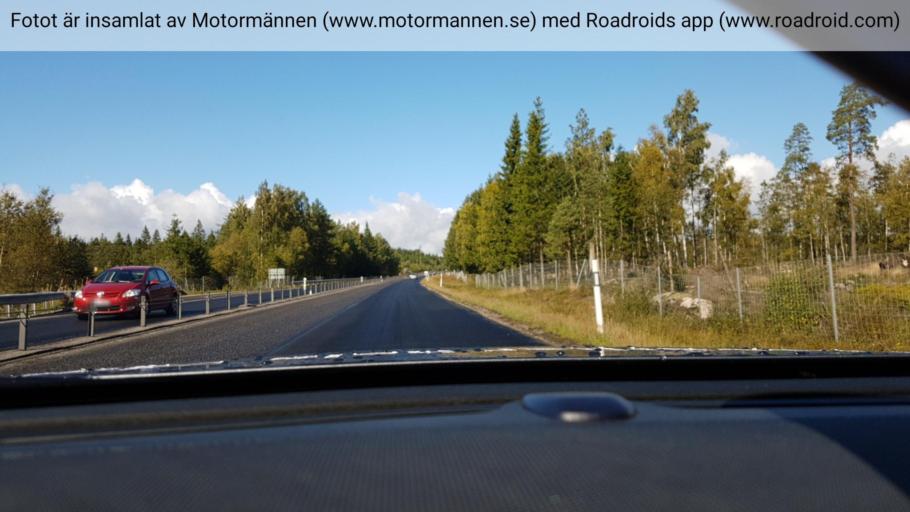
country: SE
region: Vaestra Goetaland
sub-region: Boras Kommun
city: Dalsjofors
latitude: 57.6278
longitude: 13.0923
